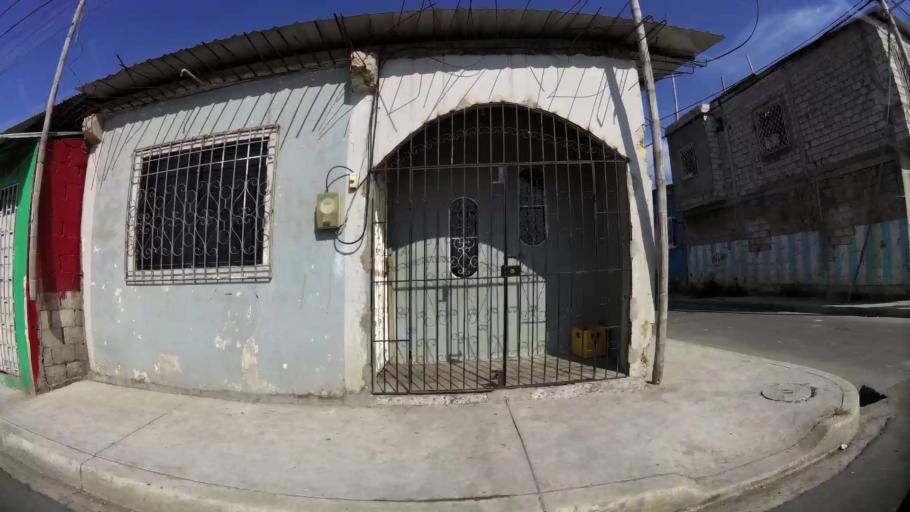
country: EC
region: Guayas
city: Eloy Alfaro
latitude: -2.0809
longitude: -79.9239
